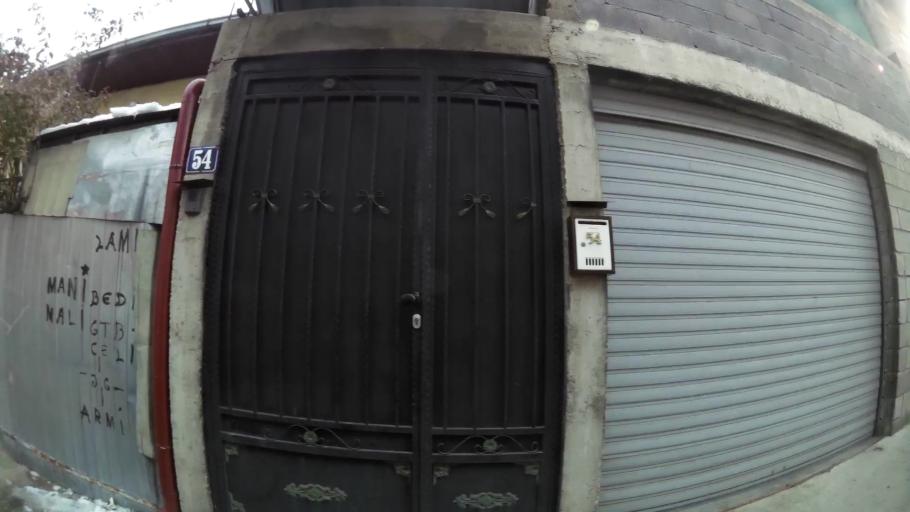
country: MK
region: Cair
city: Cair
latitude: 42.0047
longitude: 21.4473
